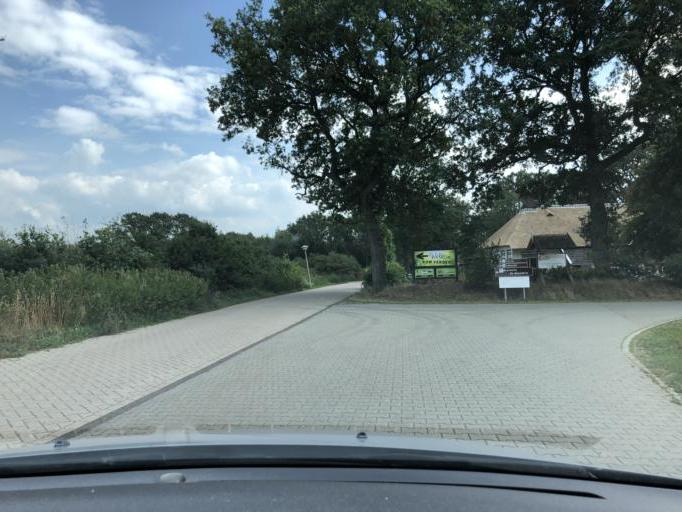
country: NL
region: Drenthe
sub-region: Gemeente De Wolden
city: Ruinen
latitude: 52.6134
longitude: 6.3700
